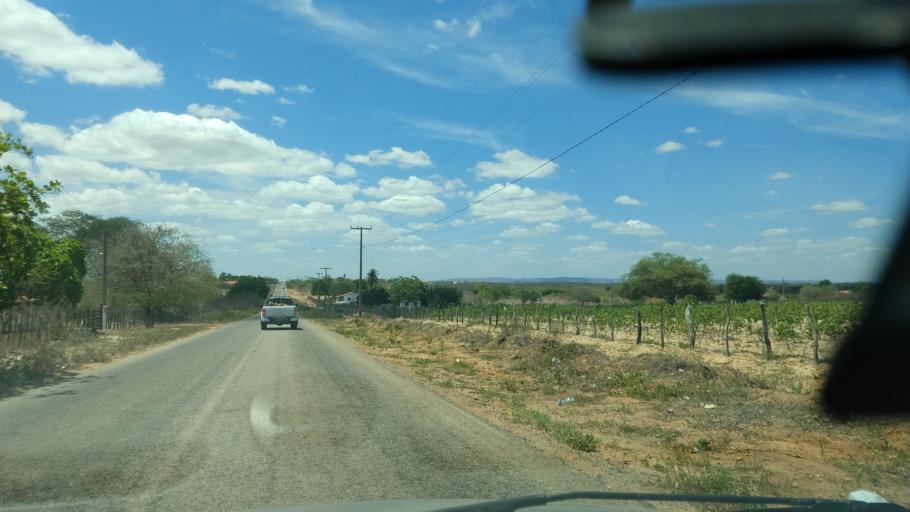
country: BR
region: Rio Grande do Norte
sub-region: Sao Paulo Do Potengi
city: Sao Paulo do Potengi
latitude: -5.9155
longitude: -35.7308
